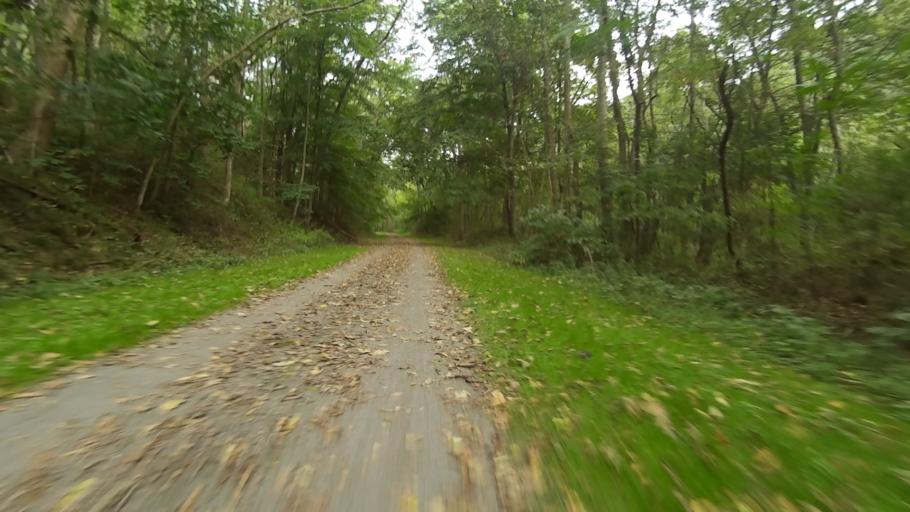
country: US
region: Pennsylvania
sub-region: Blair County
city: Williamsburg
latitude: 40.4890
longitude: -78.1671
